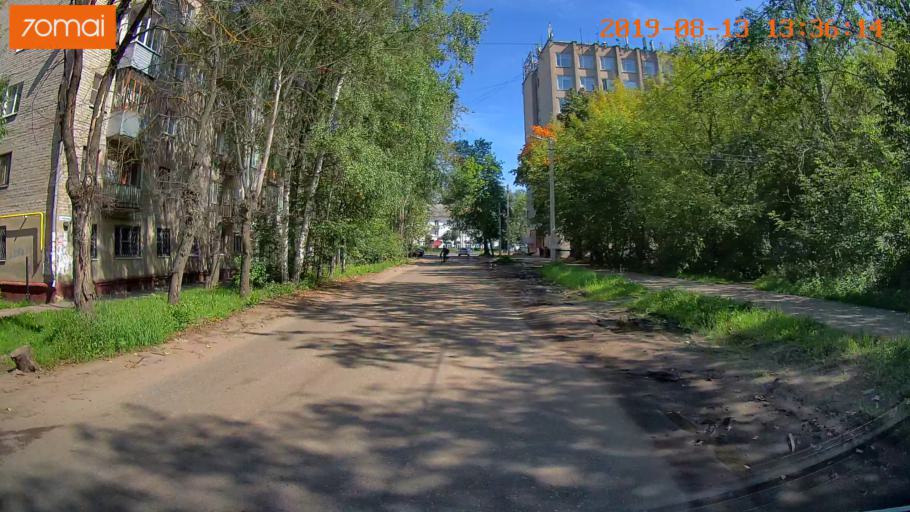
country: RU
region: Ivanovo
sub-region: Gorod Ivanovo
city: Ivanovo
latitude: 56.9691
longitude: 40.9714
